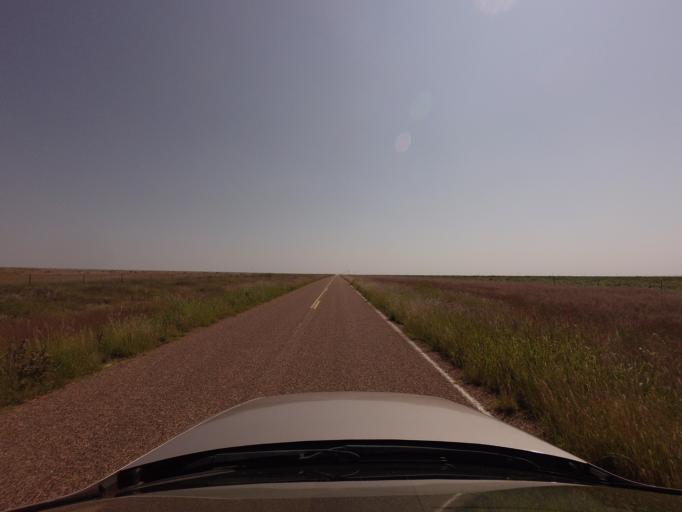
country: US
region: New Mexico
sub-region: Curry County
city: Cannon Air Force Base
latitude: 34.6330
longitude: -103.3967
